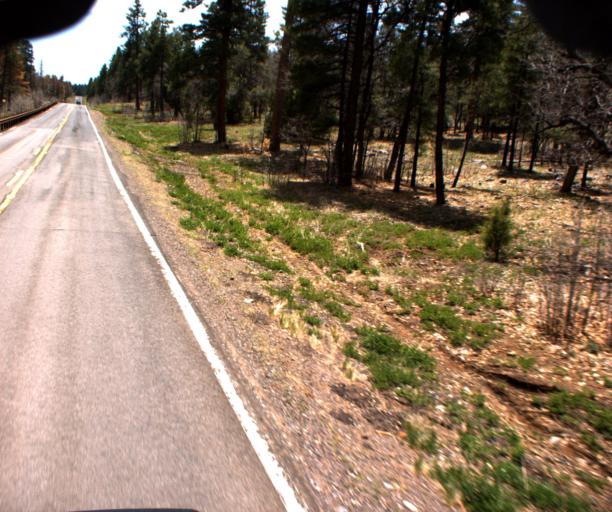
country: US
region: Arizona
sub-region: Coconino County
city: Kachina Village
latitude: 35.0552
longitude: -111.7326
